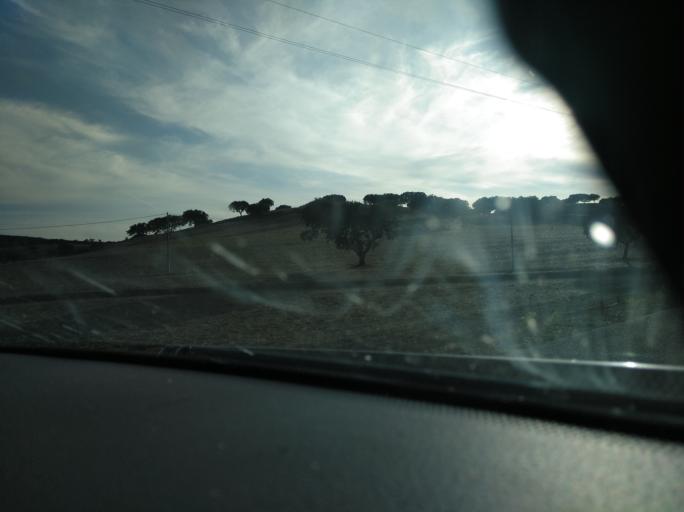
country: PT
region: Evora
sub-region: Estremoz
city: Estremoz
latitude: 38.9529
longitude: -7.5319
